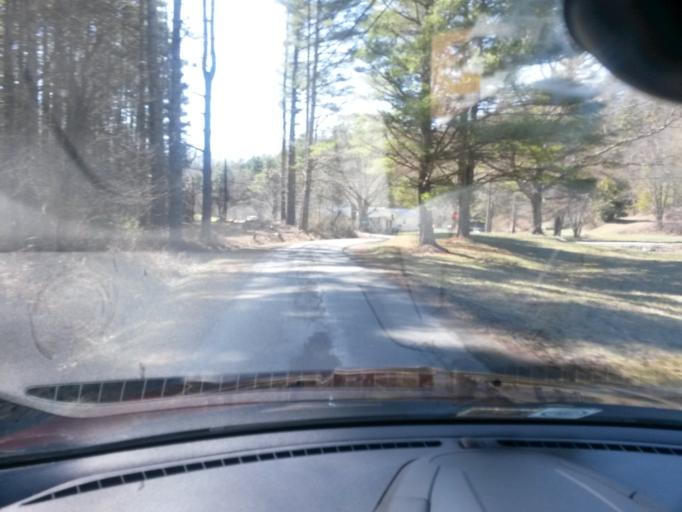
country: US
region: West Virginia
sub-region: Greenbrier County
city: White Sulphur Springs
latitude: 37.6816
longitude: -80.3397
